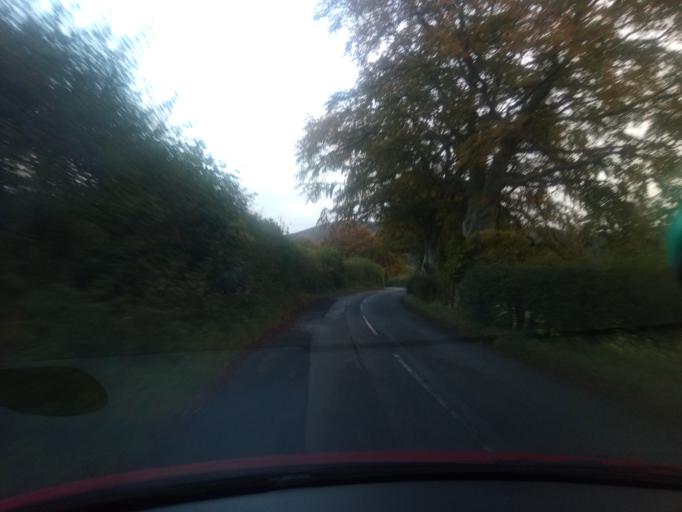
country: GB
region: Scotland
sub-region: The Scottish Borders
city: Hawick
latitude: 55.3429
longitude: -2.6514
